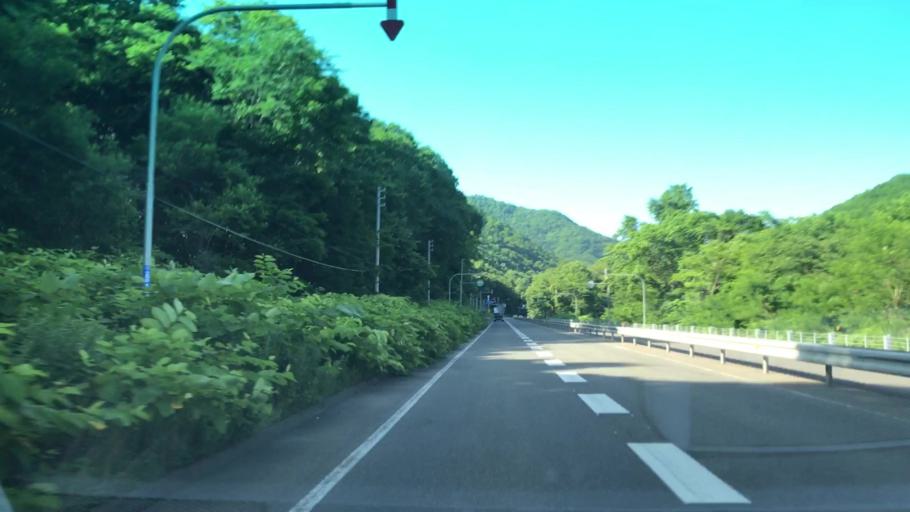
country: JP
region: Hokkaido
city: Iwanai
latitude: 43.0139
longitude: 140.6660
